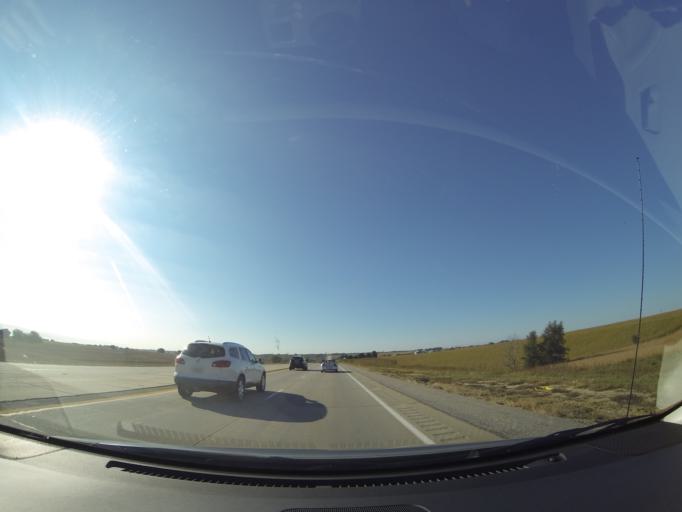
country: US
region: Nebraska
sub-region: Sarpy County
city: Gretna
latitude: 41.1855
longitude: -96.2342
